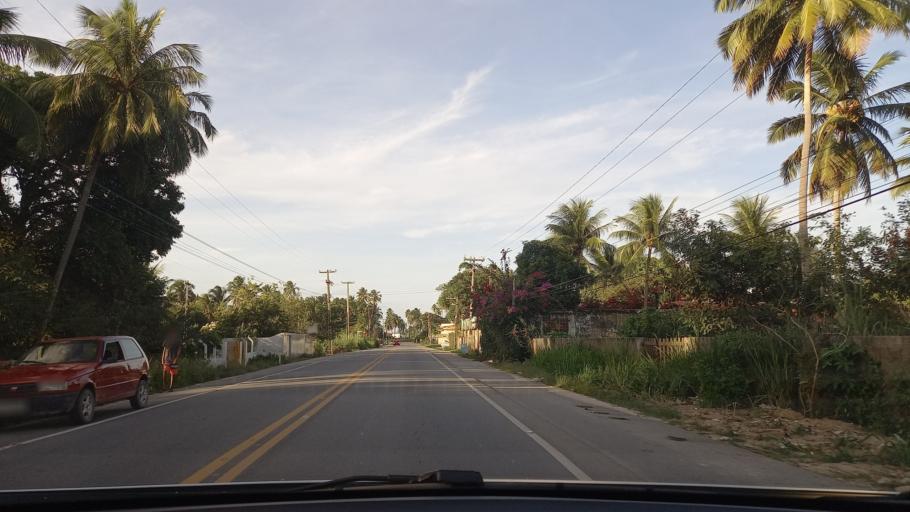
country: BR
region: Pernambuco
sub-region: Sao Jose Da Coroa Grande
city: Sao Jose da Coroa Grande
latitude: -8.9194
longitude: -35.1561
